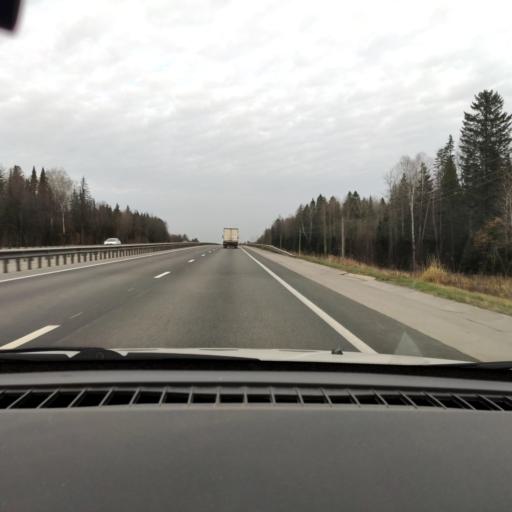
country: RU
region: Perm
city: Ferma
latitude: 58.0222
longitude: 56.4208
